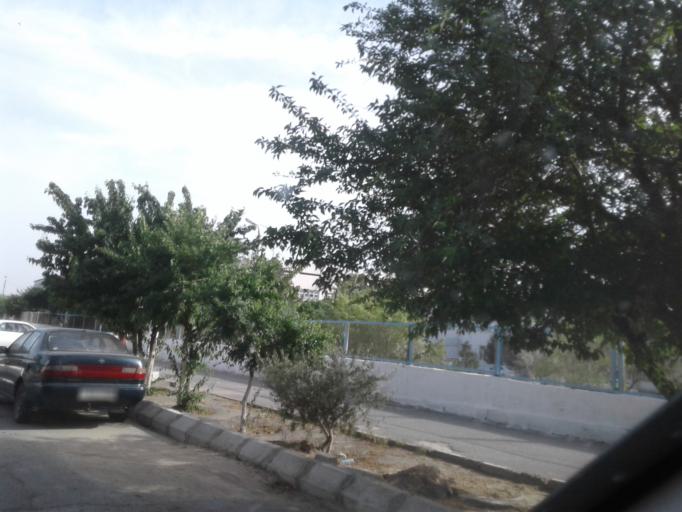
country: TM
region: Balkan
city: Turkmenbasy
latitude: 39.9966
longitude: 52.9707
